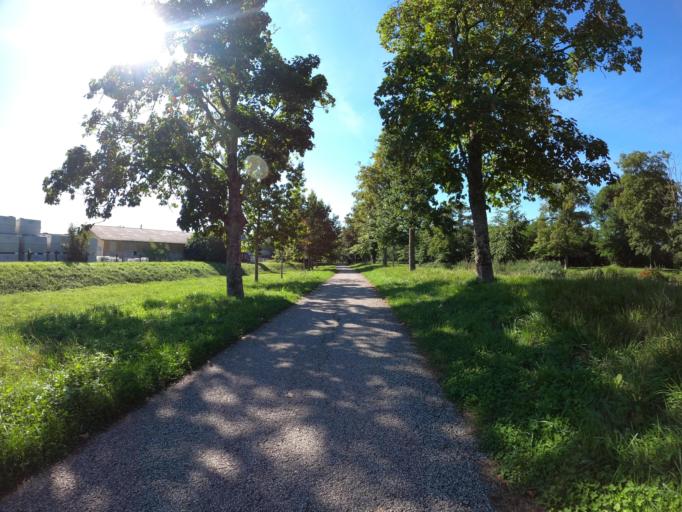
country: FR
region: Aquitaine
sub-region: Departement du Lot-et-Garonne
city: Bon-Encontre
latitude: 44.1890
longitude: 0.6521
